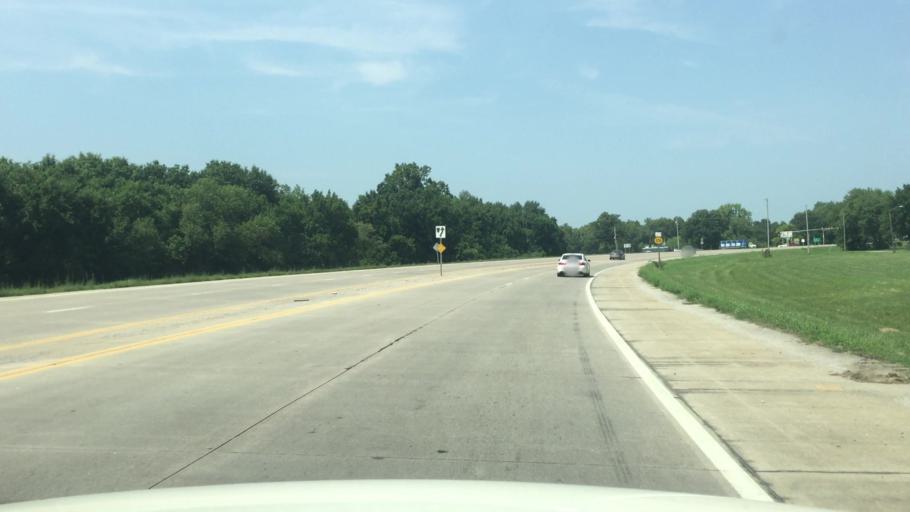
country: US
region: Kansas
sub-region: Crawford County
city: Pittsburg
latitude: 37.4078
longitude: -94.7247
